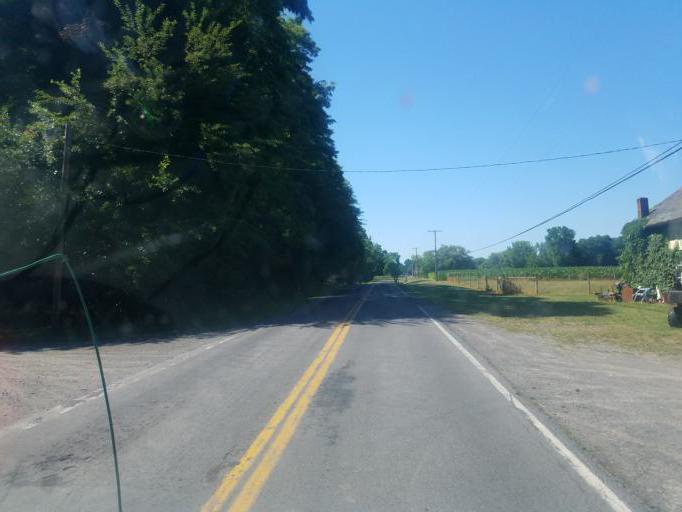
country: US
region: New York
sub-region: Ontario County
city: Geneva
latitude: 42.9225
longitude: -76.9969
